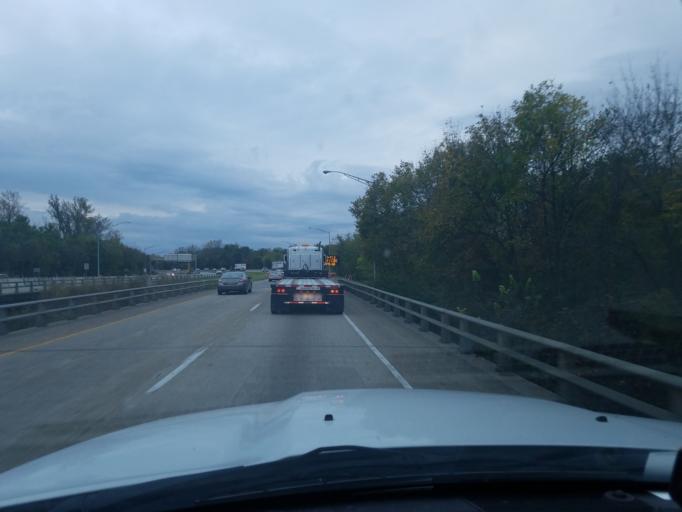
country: US
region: Indiana
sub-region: Vanderburgh County
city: Evansville
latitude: 37.9361
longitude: -87.5469
